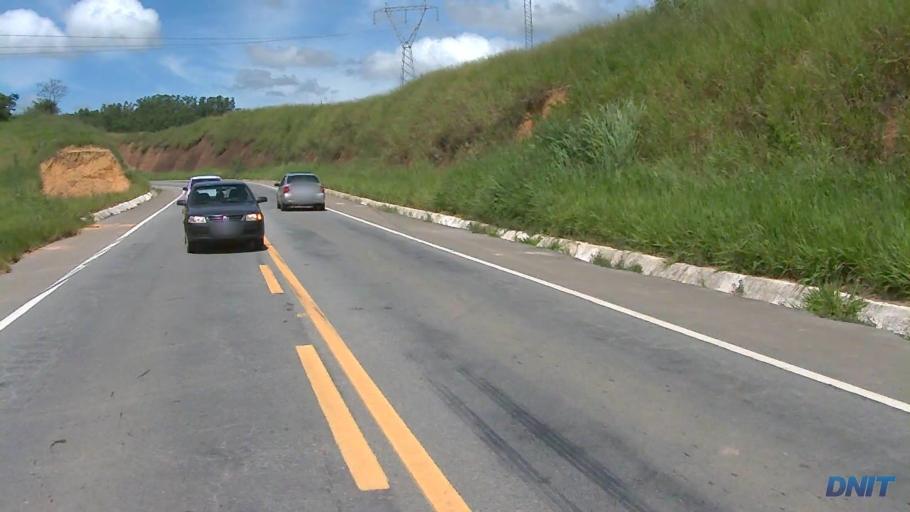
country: BR
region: Minas Gerais
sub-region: Belo Oriente
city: Belo Oriente
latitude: -19.0907
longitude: -42.1889
